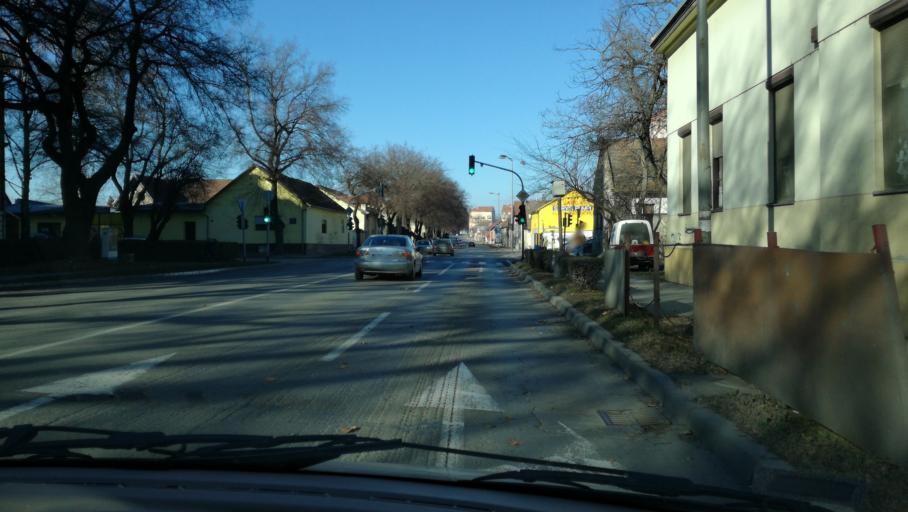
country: RS
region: Autonomna Pokrajina Vojvodina
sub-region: Severnobacki Okrug
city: Subotica
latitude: 46.0896
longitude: 19.6658
